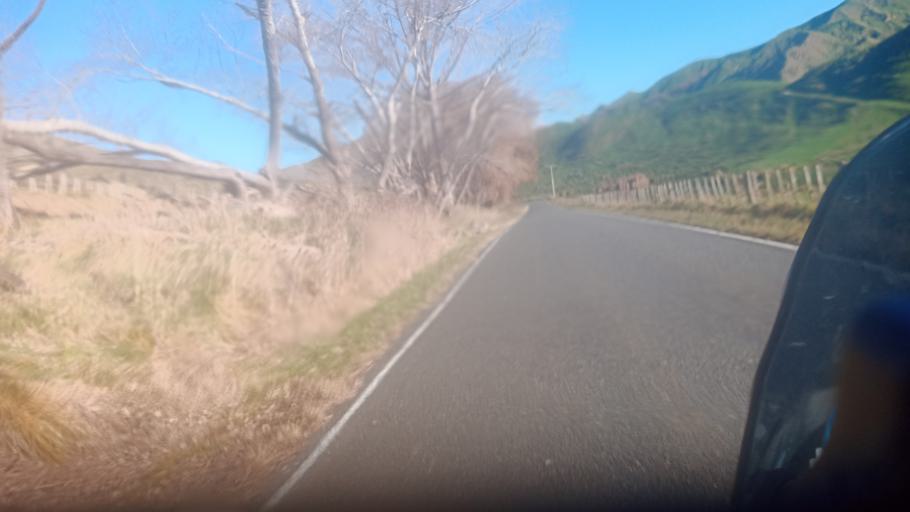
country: NZ
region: Gisborne
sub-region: Gisborne District
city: Gisborne
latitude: -38.5668
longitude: 177.6004
